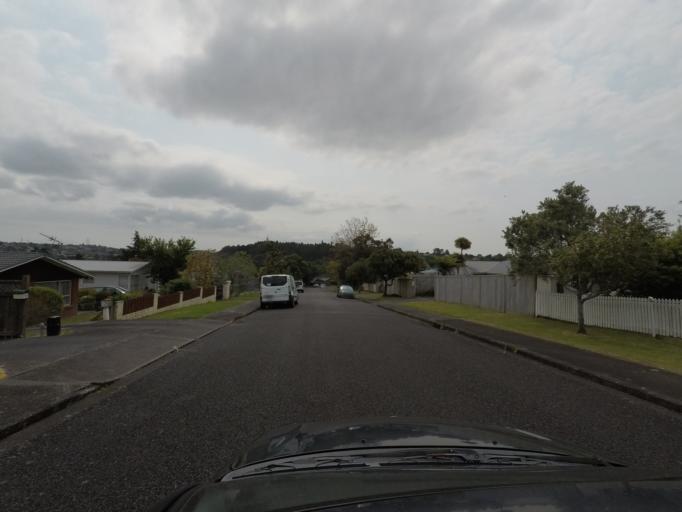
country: NZ
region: Auckland
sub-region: Auckland
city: Rosebank
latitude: -36.8419
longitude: 174.6362
